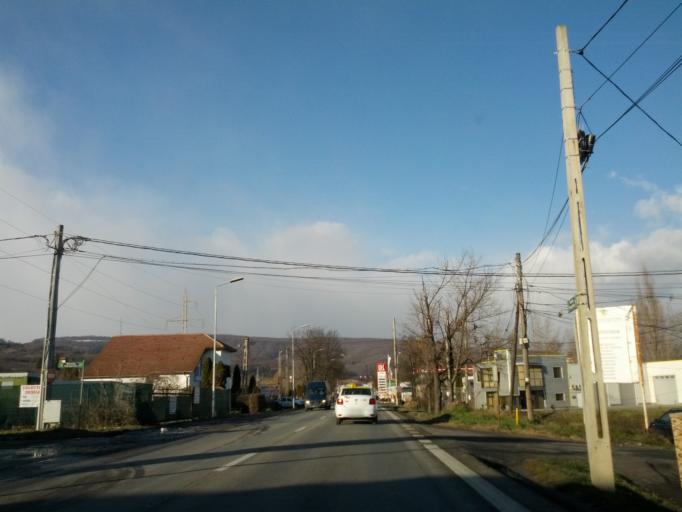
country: RO
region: Valcea
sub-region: Comuna Bujoreni
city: Bujoreni
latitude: 45.1243
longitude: 24.3682
